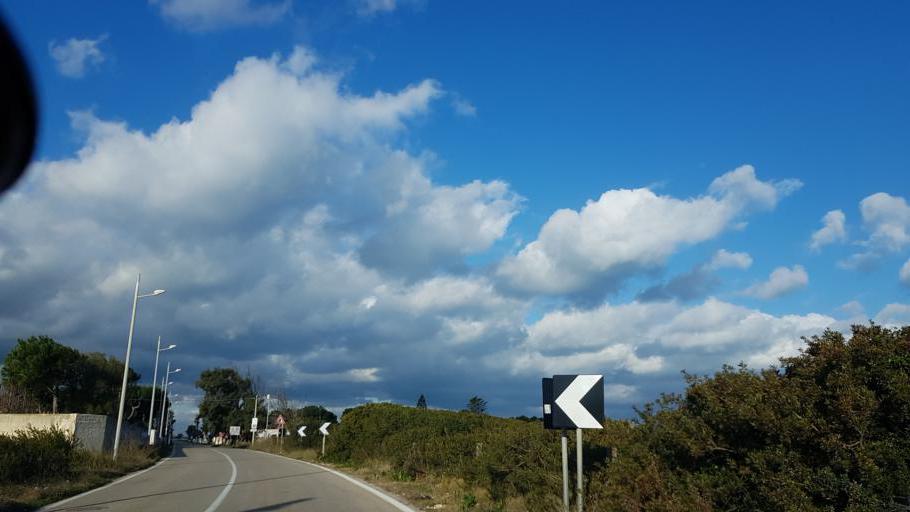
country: IT
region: Apulia
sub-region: Provincia di Brindisi
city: Materdomini
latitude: 40.6782
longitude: 17.9397
